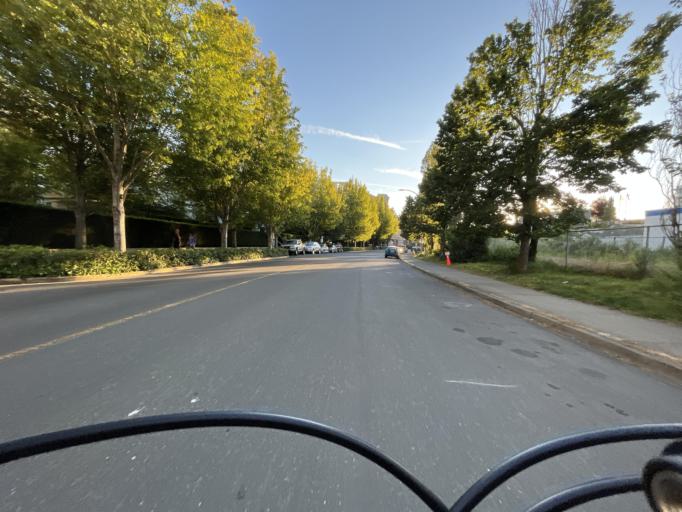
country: CA
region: British Columbia
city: Victoria
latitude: 48.4273
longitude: -123.3785
